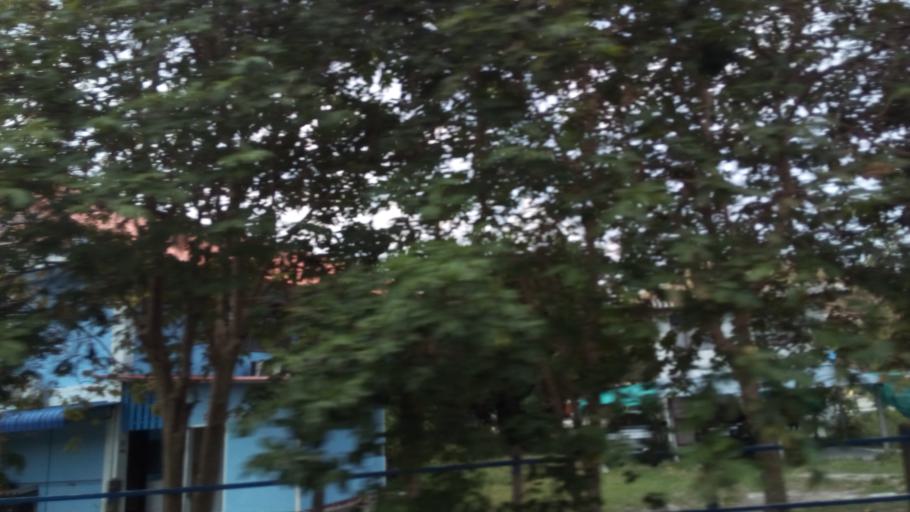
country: TH
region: Sara Buri
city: Saraburi
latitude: 14.4567
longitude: 100.9470
